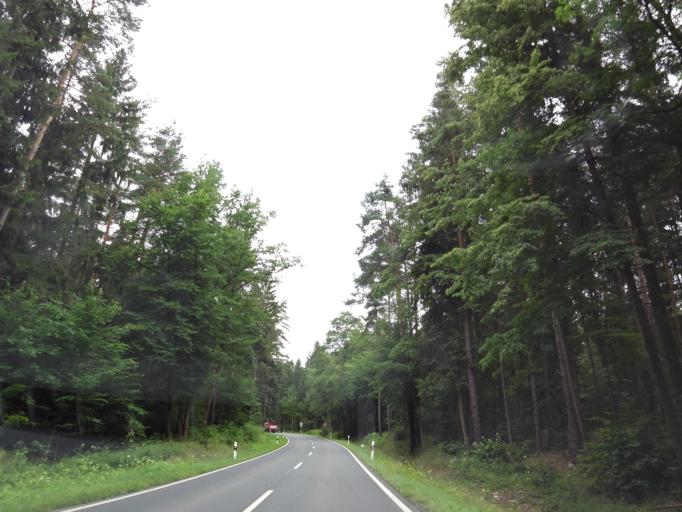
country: DE
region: Thuringia
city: Bad Klosterlausnitz
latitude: 50.9278
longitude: 11.8662
